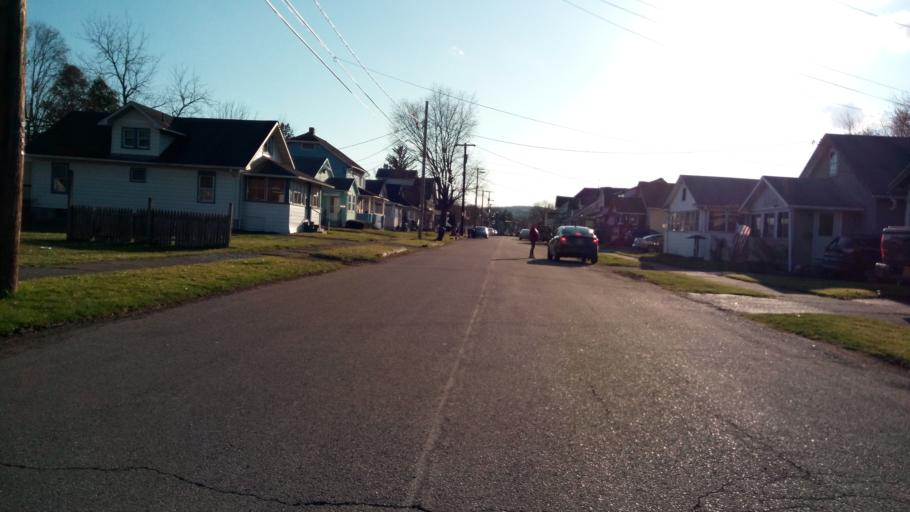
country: US
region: New York
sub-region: Chemung County
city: Elmira
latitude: 42.0778
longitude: -76.7850
